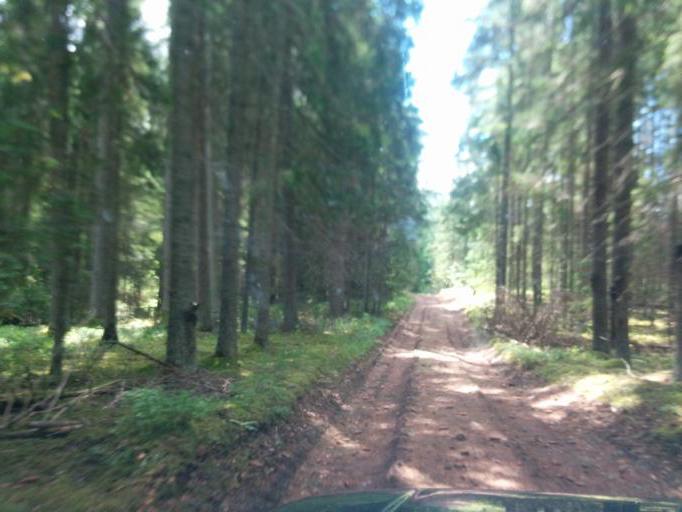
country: LV
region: Vilaka
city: Vilaka
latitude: 57.3349
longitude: 27.6925
